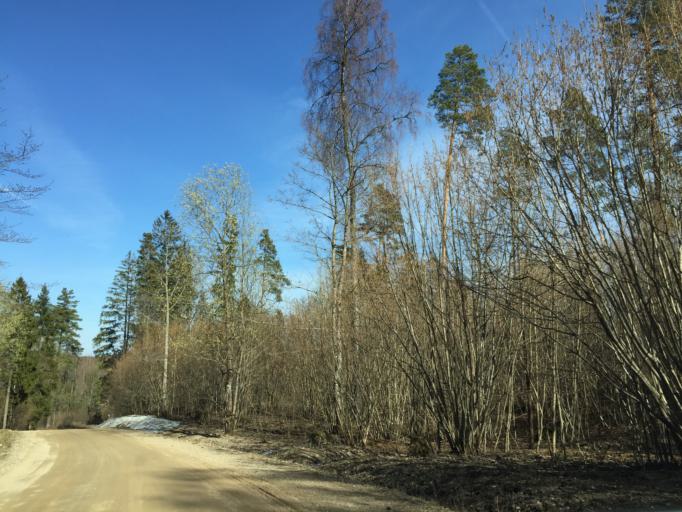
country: EE
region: Vorumaa
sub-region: Antsla vald
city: Vana-Antsla
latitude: 57.9941
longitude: 26.3765
